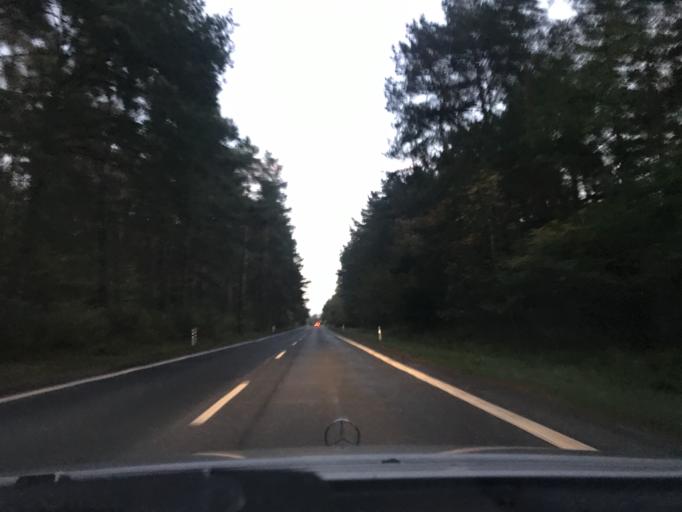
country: DE
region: Mecklenburg-Vorpommern
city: Karlshagen
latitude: 54.1244
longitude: 13.8251
